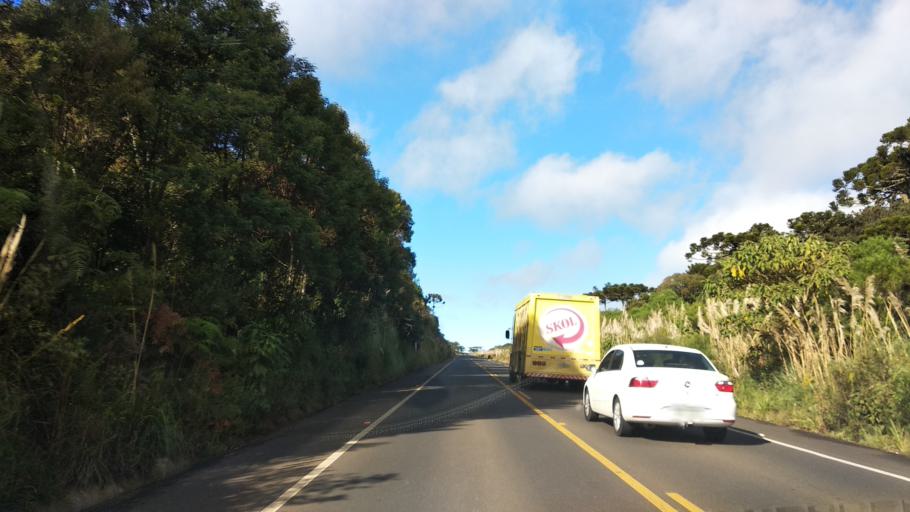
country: BR
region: Santa Catarina
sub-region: Lages
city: Lages
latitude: -27.9621
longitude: -50.0979
